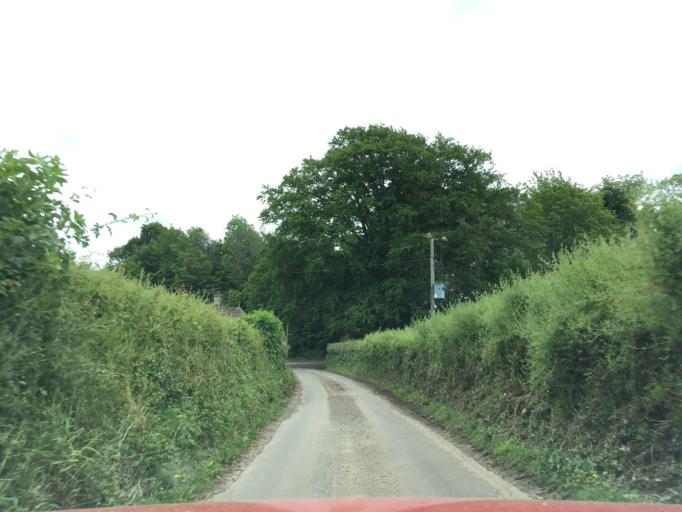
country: GB
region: England
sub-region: Wiltshire
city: Nettleton
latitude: 51.5153
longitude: -2.2311
